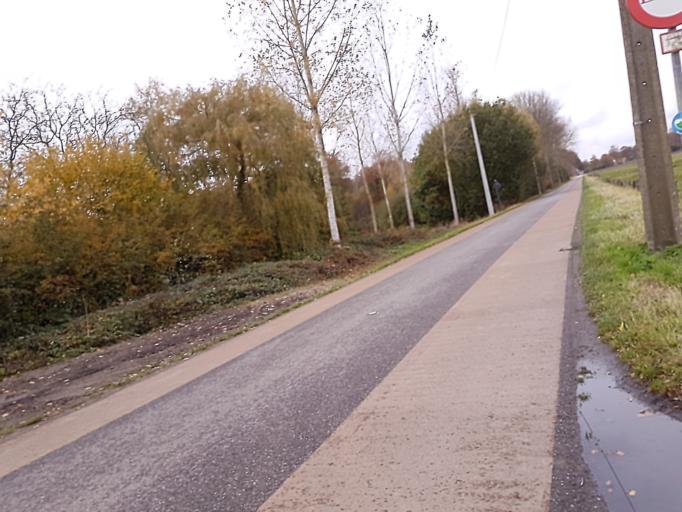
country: BE
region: Flanders
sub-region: Provincie Antwerpen
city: Boechout
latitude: 51.1531
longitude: 4.5030
